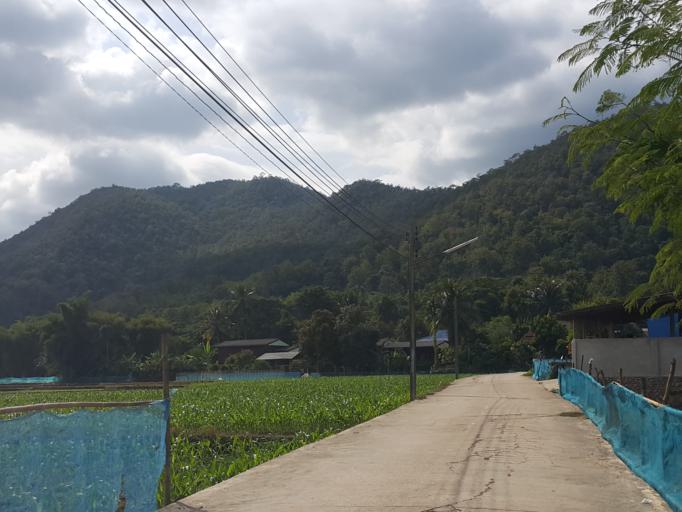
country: TH
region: Lampang
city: Chae Hom
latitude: 18.5628
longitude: 99.4501
